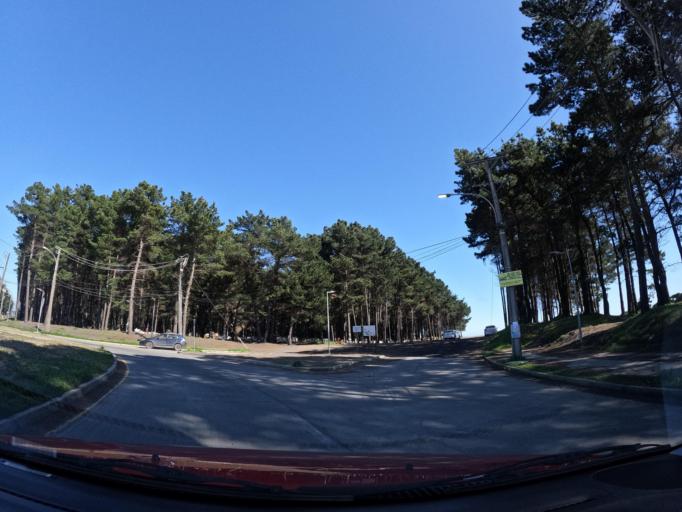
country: CL
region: Biobio
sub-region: Provincia de Concepcion
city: Concepcion
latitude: -36.8818
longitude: -73.1495
